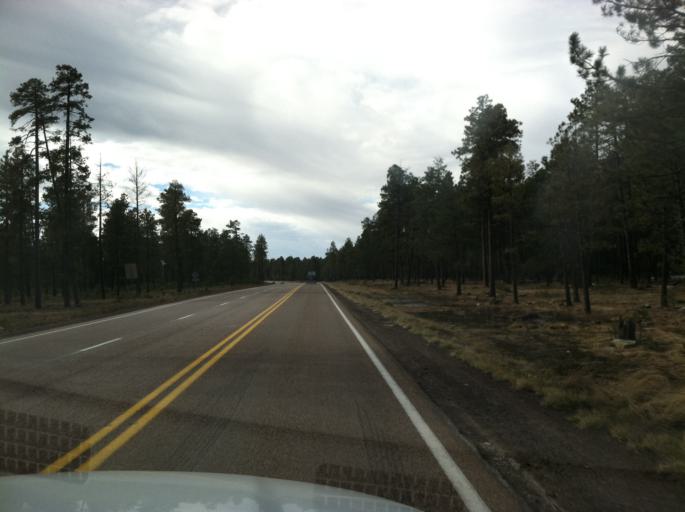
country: US
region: Arizona
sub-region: Navajo County
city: Heber-Overgaard
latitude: 34.3129
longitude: -110.8516
